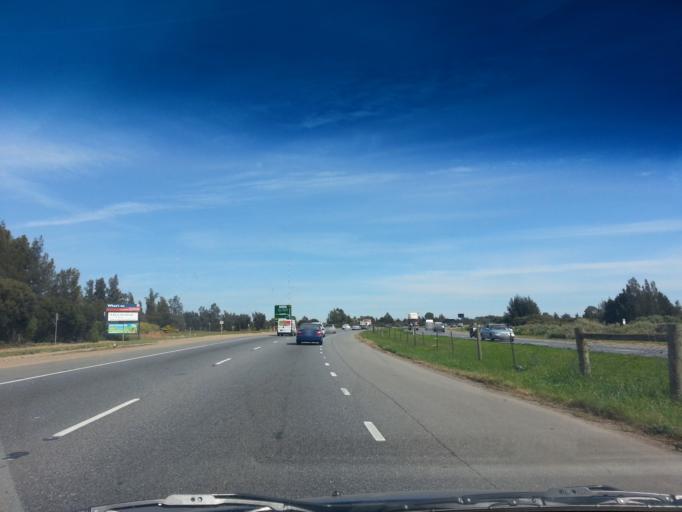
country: AU
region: South Australia
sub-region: Port Adelaide Enfield
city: Enfield
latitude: -34.8322
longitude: 138.5822
